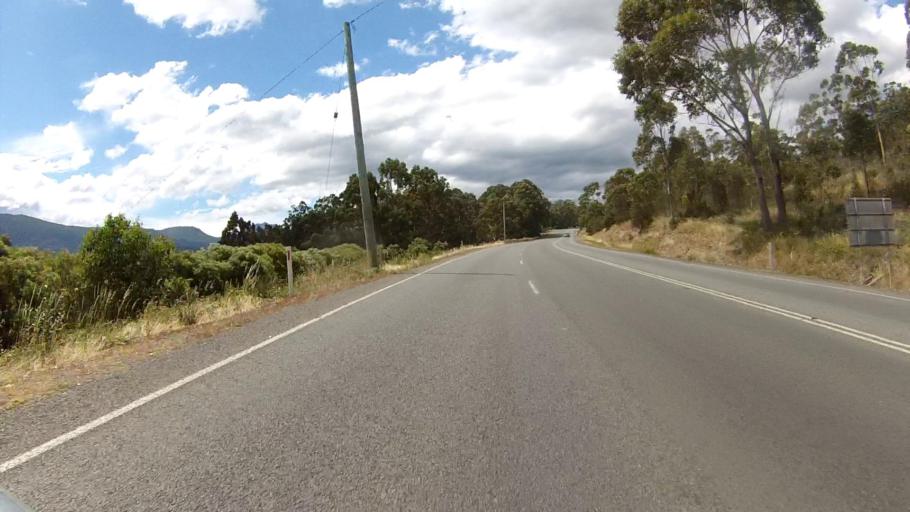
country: AU
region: Tasmania
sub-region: Huon Valley
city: Huonville
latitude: -42.9793
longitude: 147.1005
